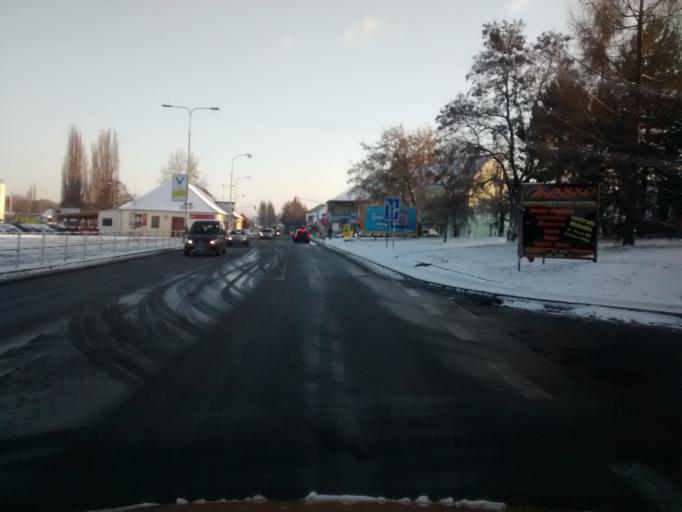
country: CZ
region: Central Bohemia
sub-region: Okres Melnik
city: Melnik
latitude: 50.3502
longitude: 14.4871
